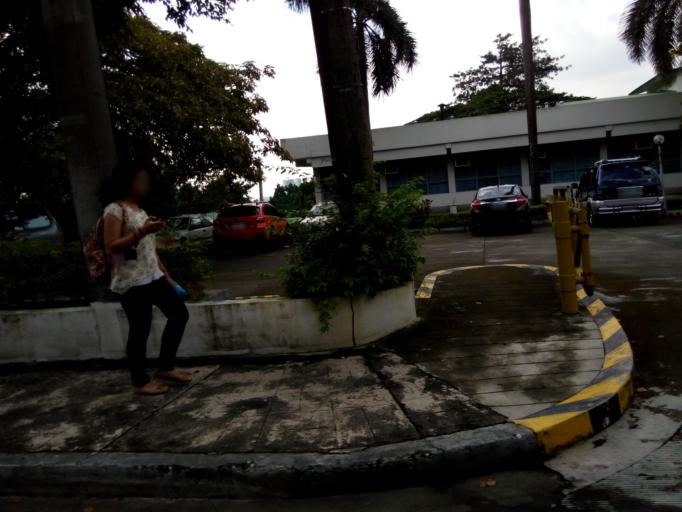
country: PH
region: Metro Manila
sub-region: Quezon City
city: Quezon City
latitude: 14.6523
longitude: 121.0690
